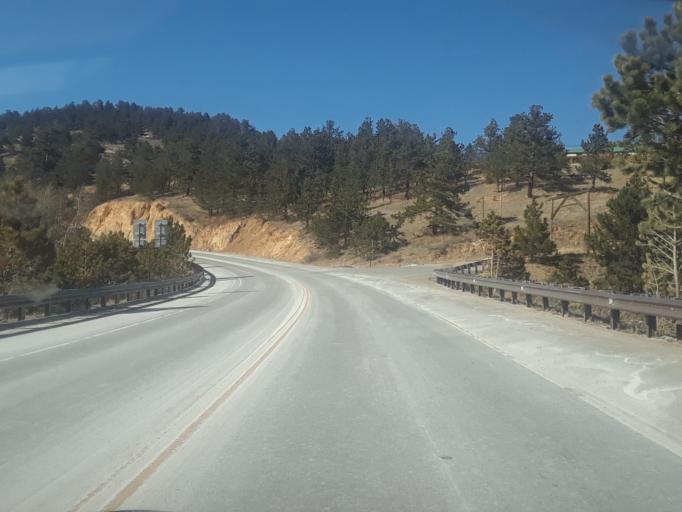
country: US
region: Colorado
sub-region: Larimer County
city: Estes Park
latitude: 40.1914
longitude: -105.5105
